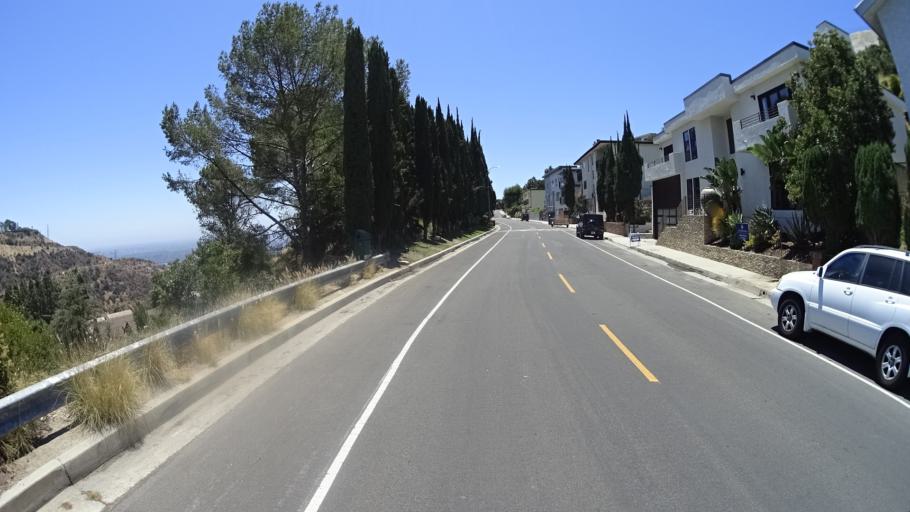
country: US
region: California
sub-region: Los Angeles County
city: West Hollywood
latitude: 34.1139
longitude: -118.3641
